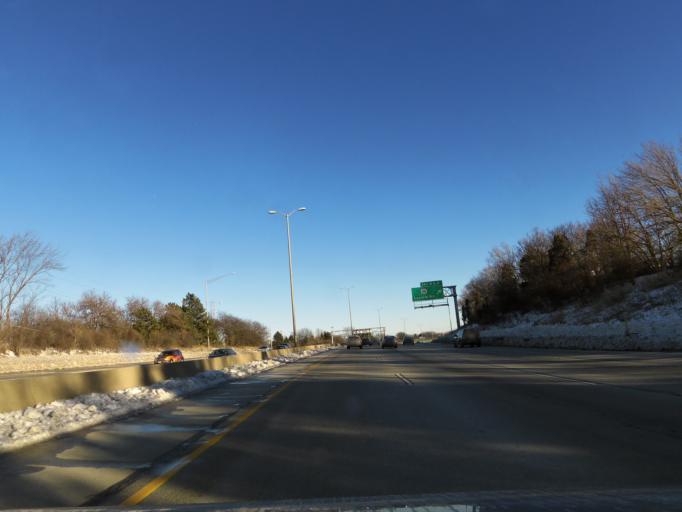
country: US
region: Wisconsin
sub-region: Milwaukee County
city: Greendale
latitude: 42.9626
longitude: -87.9745
